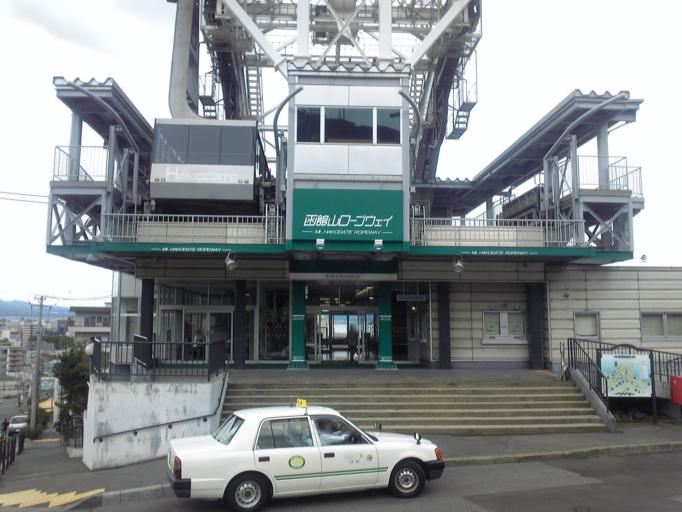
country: JP
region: Hokkaido
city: Hakodate
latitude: 41.7609
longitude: 140.7144
